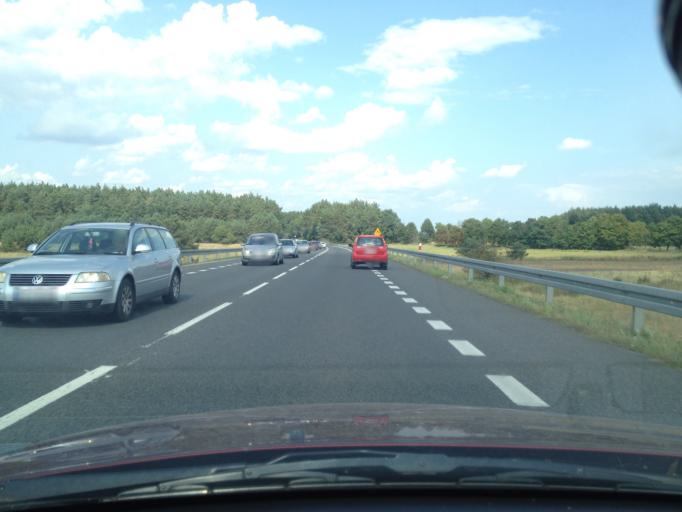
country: PL
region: West Pomeranian Voivodeship
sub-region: Powiat goleniowski
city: Przybiernow
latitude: 53.7650
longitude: 14.7801
